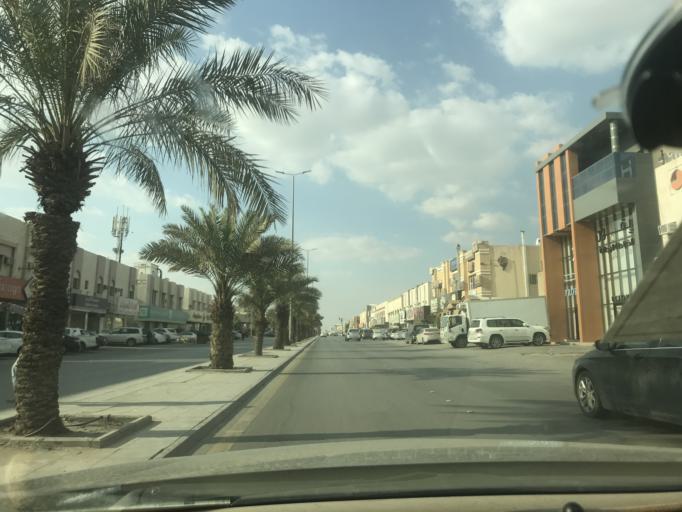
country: SA
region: Ar Riyad
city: Riyadh
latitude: 24.7347
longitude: 46.7633
